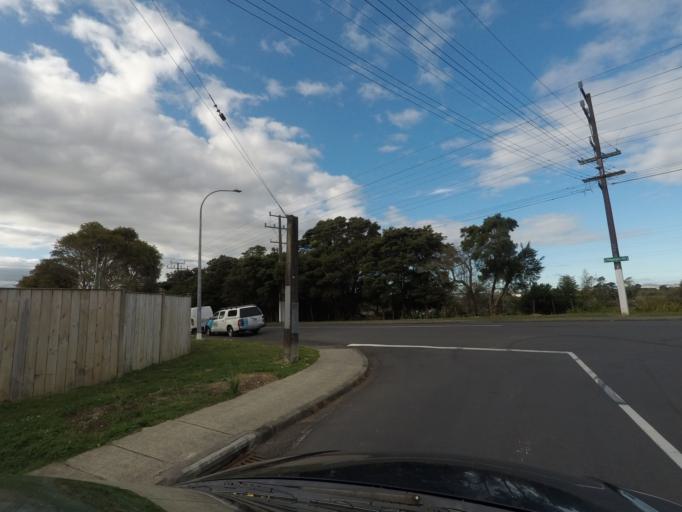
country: NZ
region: Auckland
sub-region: Auckland
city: Rosebank
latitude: -36.8835
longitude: 174.6572
